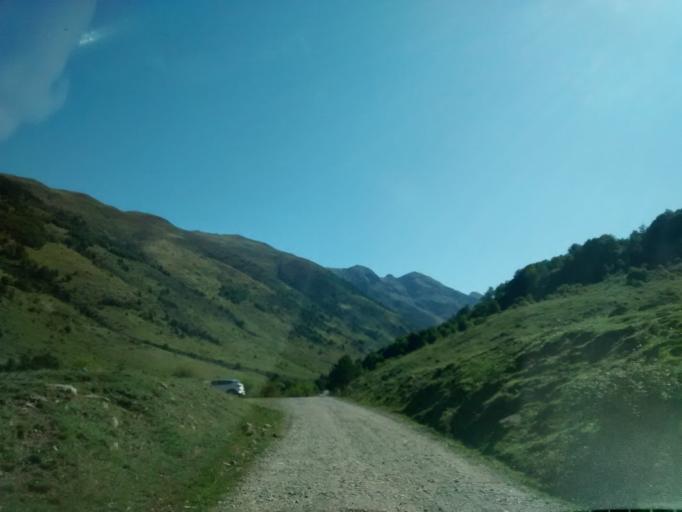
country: ES
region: Aragon
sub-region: Provincia de Huesca
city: Aragues del Puerto
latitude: 42.8532
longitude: -0.6882
